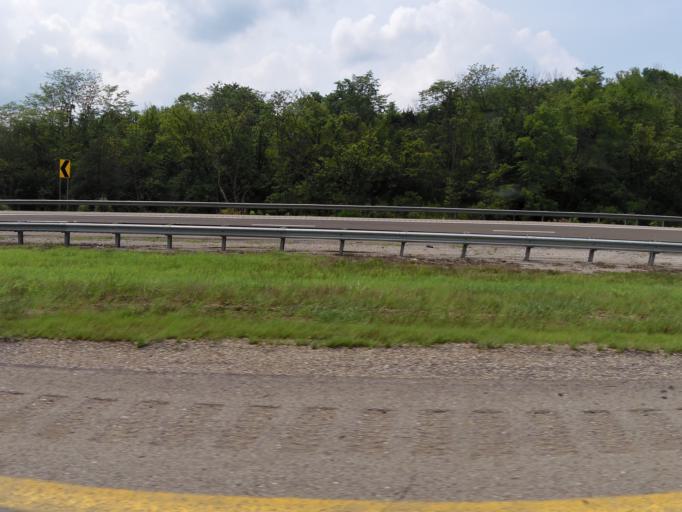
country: US
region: Kentucky
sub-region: Gallatin County
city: Warsaw
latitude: 38.7553
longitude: -84.8071
